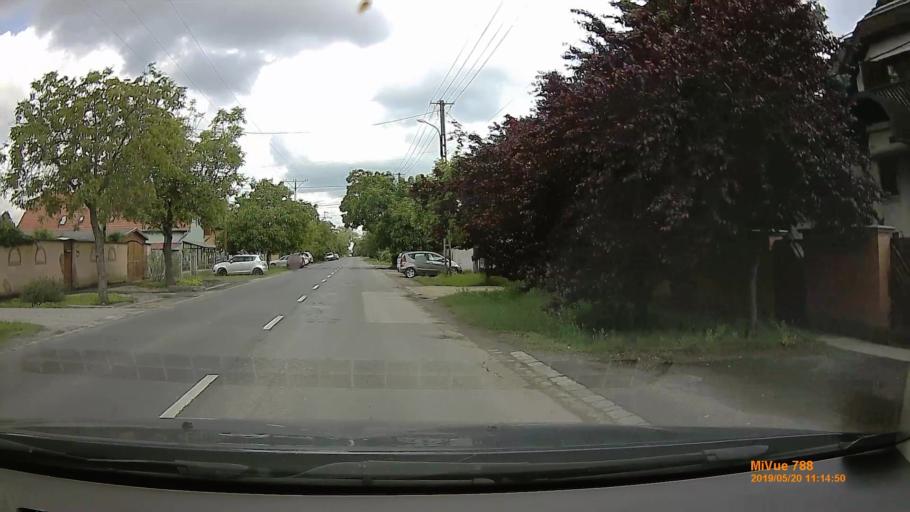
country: HU
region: Pest
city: Ecser
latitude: 47.4642
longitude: 19.2974
